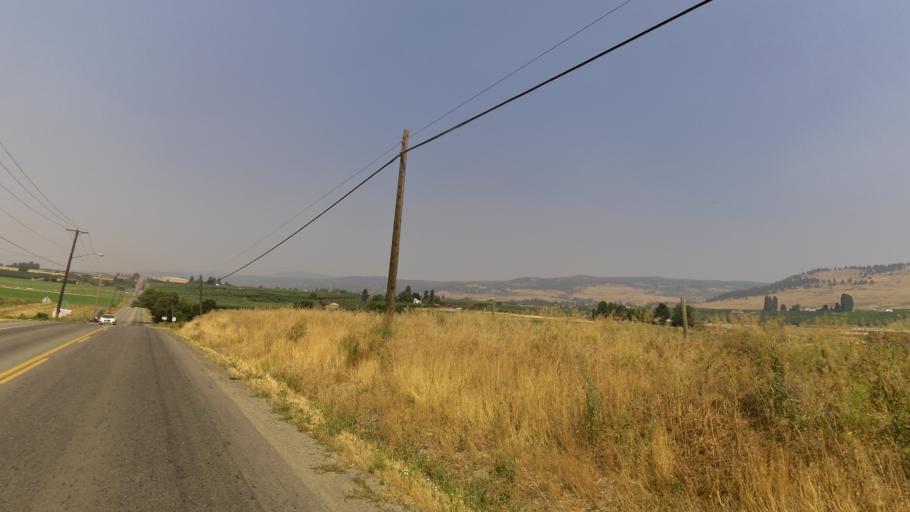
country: CA
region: British Columbia
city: Kelowna
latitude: 49.9206
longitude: -119.3642
